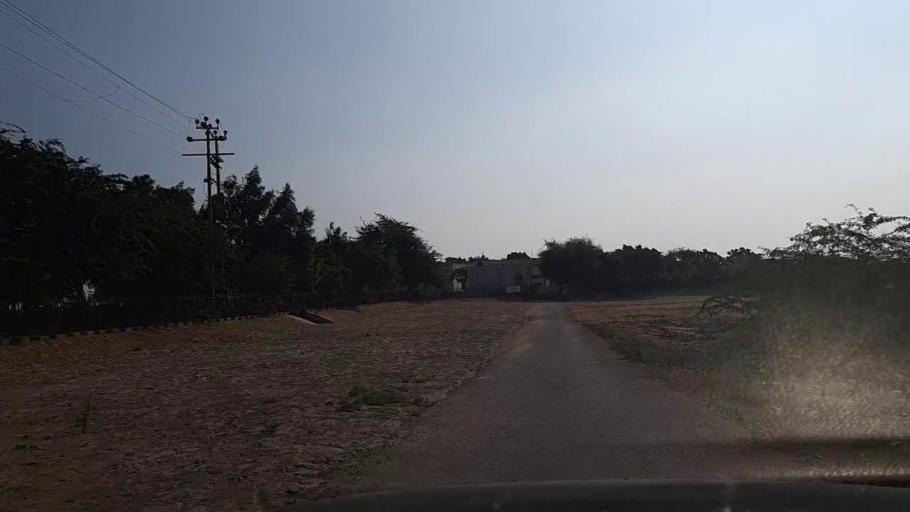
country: PK
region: Sindh
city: Gharo
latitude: 24.7562
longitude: 67.5237
